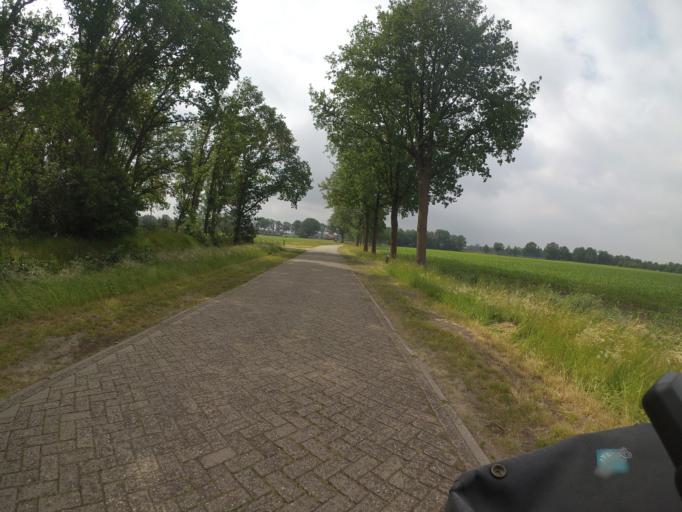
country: NL
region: Drenthe
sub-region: Gemeente Westerveld
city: Dwingeloo
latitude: 52.8378
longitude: 6.2979
